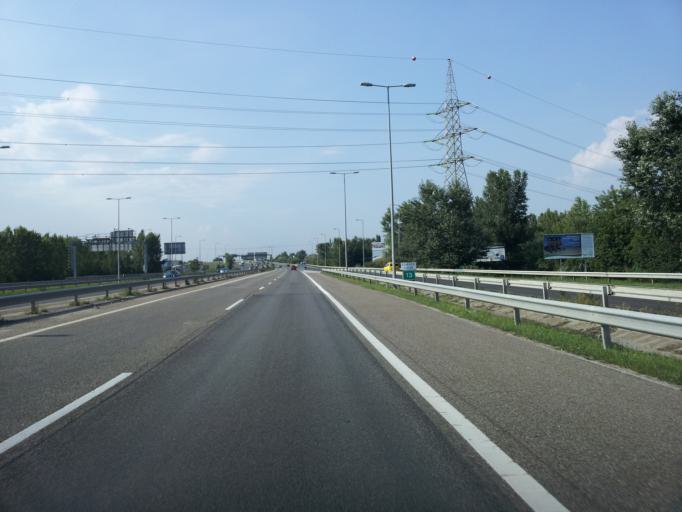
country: HU
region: Budapest
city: Budapest XIX. keruelet
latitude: 47.4271
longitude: 19.1511
